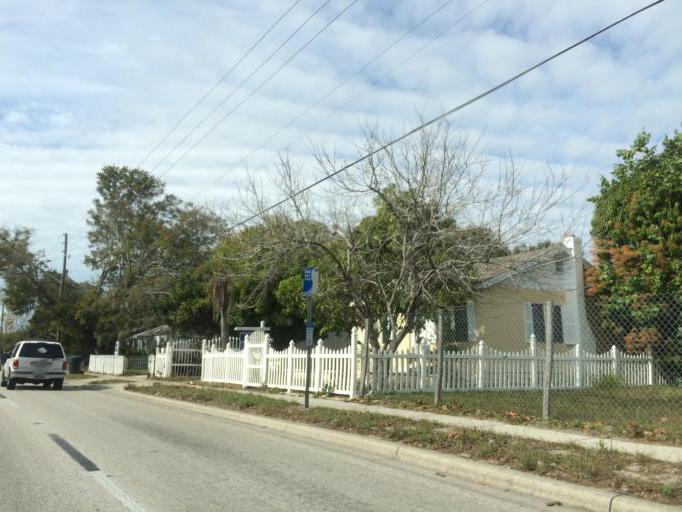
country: US
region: Florida
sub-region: Pinellas County
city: Lealman
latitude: 27.8066
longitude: -82.6734
